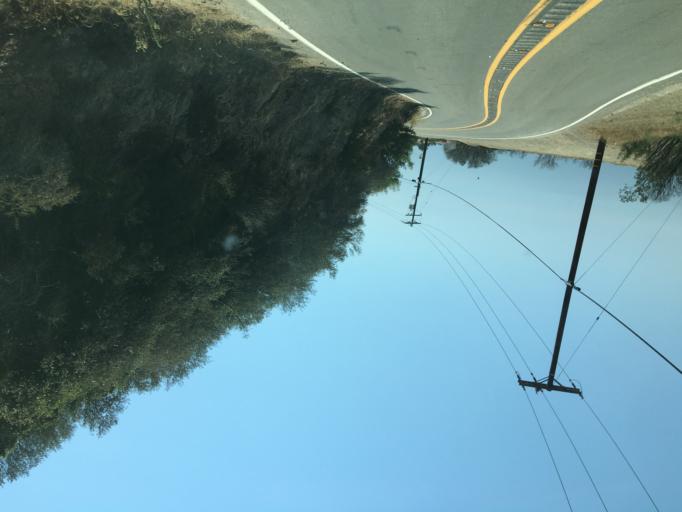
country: US
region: California
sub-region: Los Angeles County
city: Las Flores
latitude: 34.0719
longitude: -118.6526
